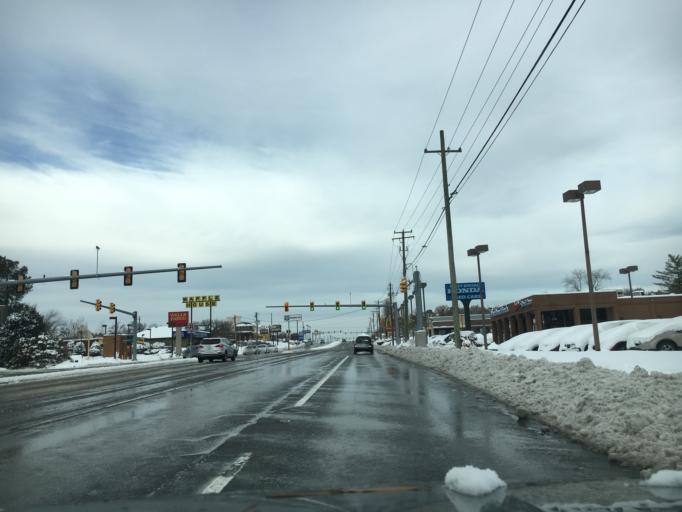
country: US
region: Virginia
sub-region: Henrico County
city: Dumbarton
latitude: 37.6102
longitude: -77.5191
